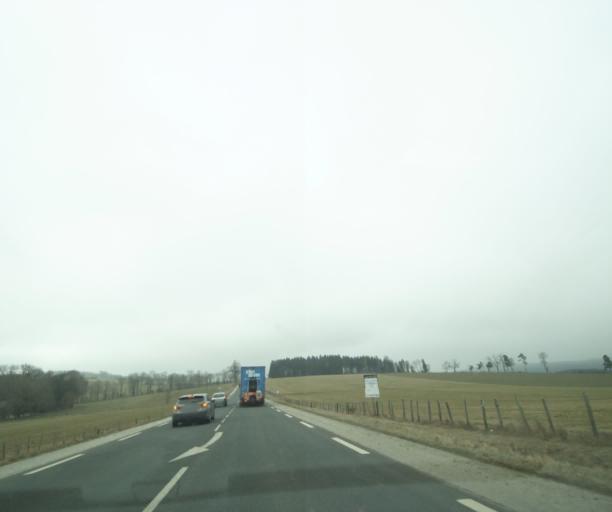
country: FR
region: Languedoc-Roussillon
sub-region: Departement de la Lozere
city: Langogne
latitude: 44.7025
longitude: 3.8187
